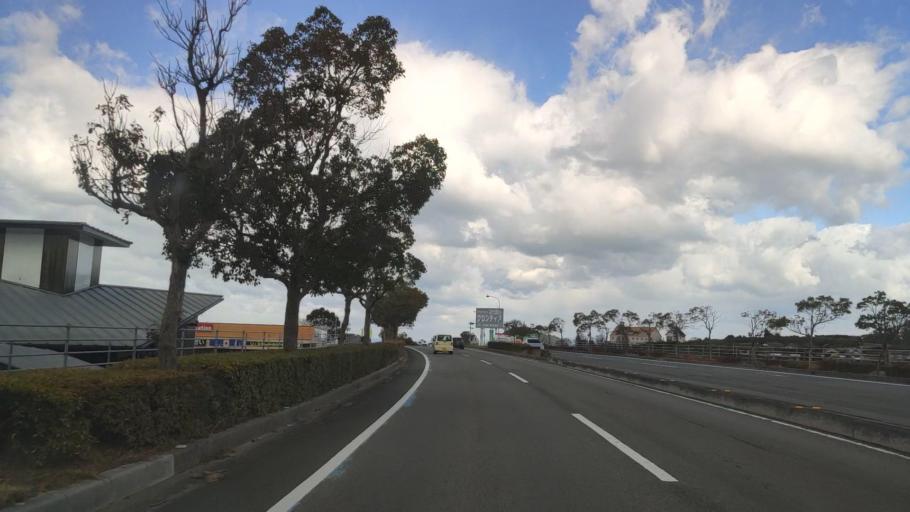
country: JP
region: Ehime
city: Hojo
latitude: 33.9461
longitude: 132.7758
